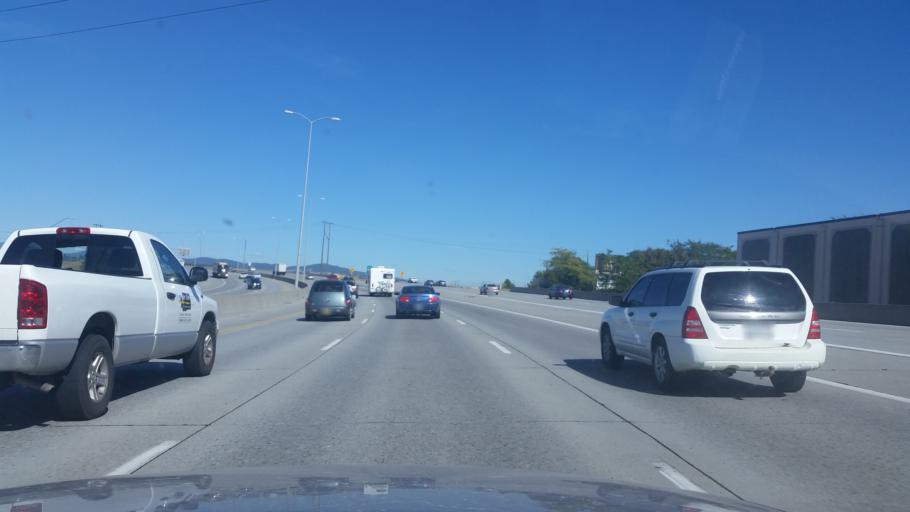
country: US
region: Washington
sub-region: Spokane County
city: Dishman
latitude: 47.6543
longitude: -117.3258
